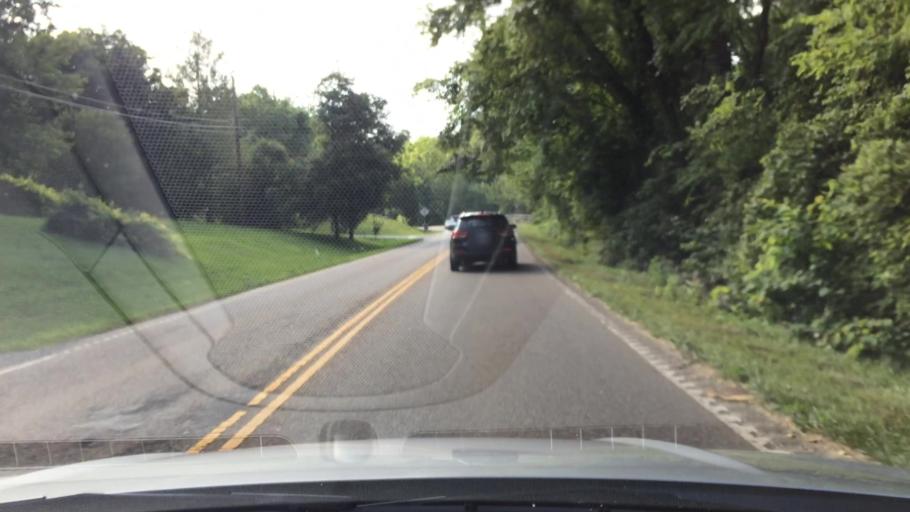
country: US
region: Tennessee
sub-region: Sevier County
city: Sevierville
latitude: 35.9235
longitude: -83.6065
